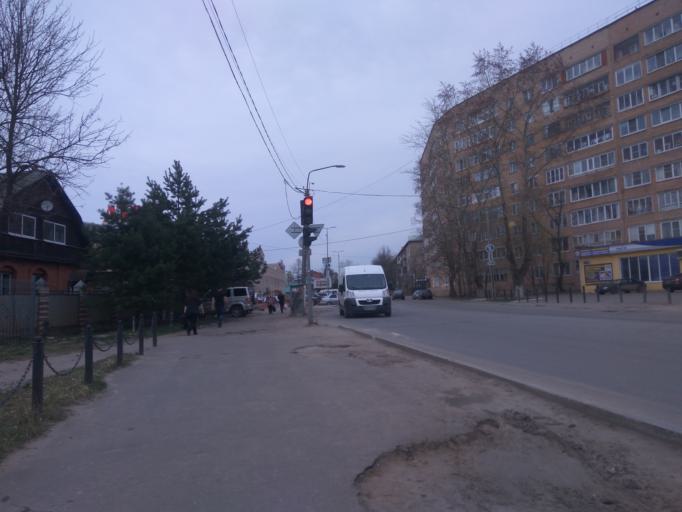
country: RU
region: Vladimir
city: Aleksandrov
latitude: 56.3979
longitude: 38.7062
